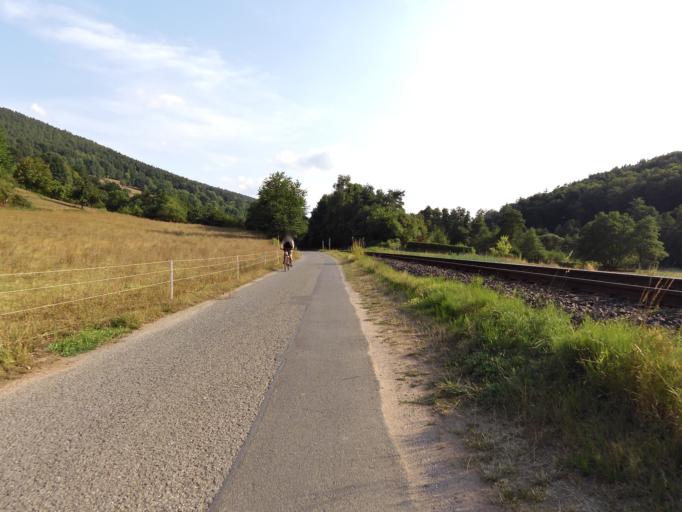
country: DE
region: Bavaria
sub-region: Regierungsbezirk Unterfranken
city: Weilbach
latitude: 49.6801
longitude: 9.2205
